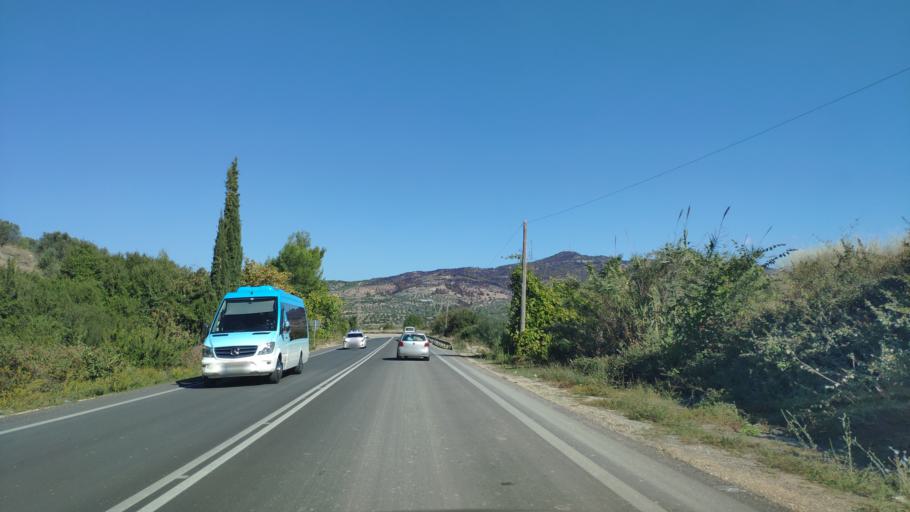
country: GR
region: Peloponnese
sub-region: Nomos Korinthias
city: Athikia
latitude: 37.8372
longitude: 22.8986
